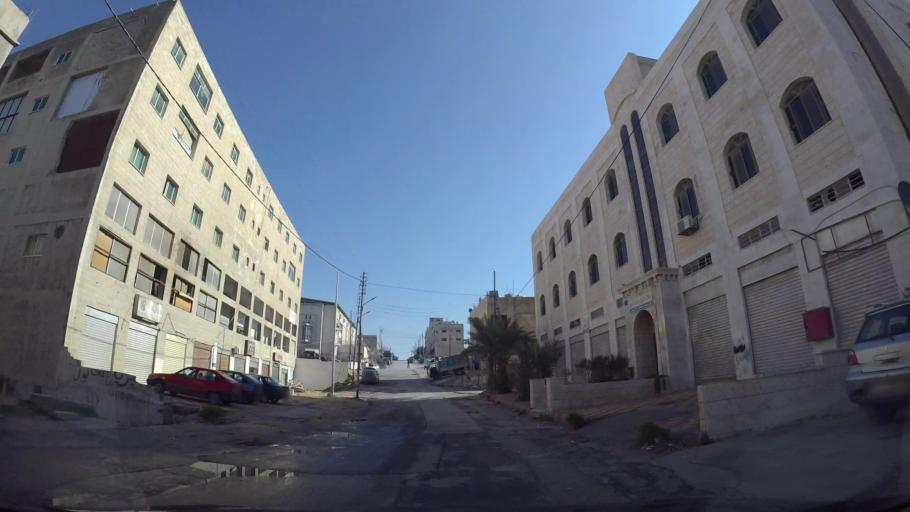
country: JO
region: Zarqa
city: Russeifa
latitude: 31.9862
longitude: 35.9968
